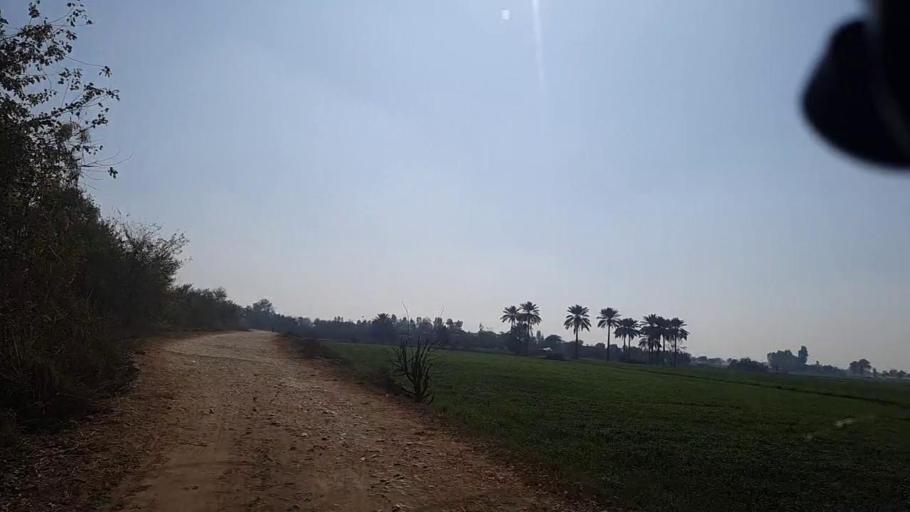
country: PK
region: Sindh
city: Khanpur
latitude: 27.7778
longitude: 69.4227
